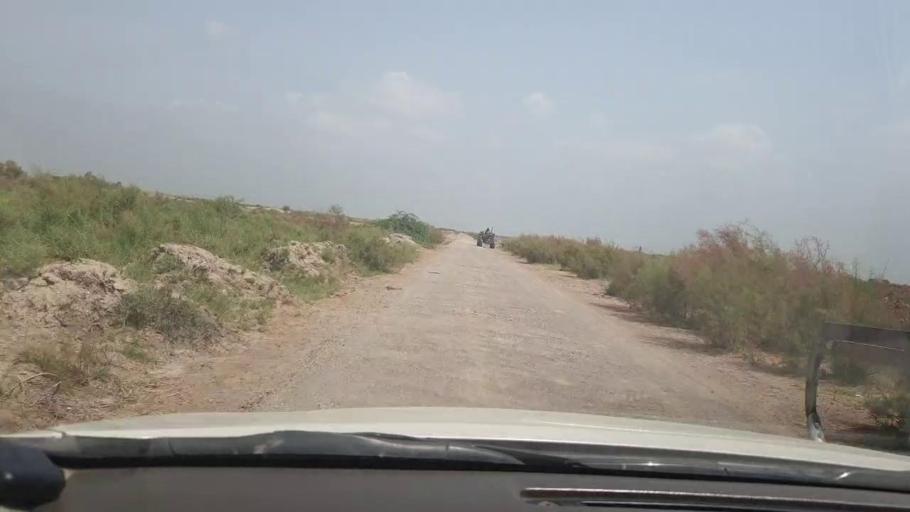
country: PK
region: Sindh
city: Garhi Yasin
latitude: 28.0139
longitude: 68.4996
